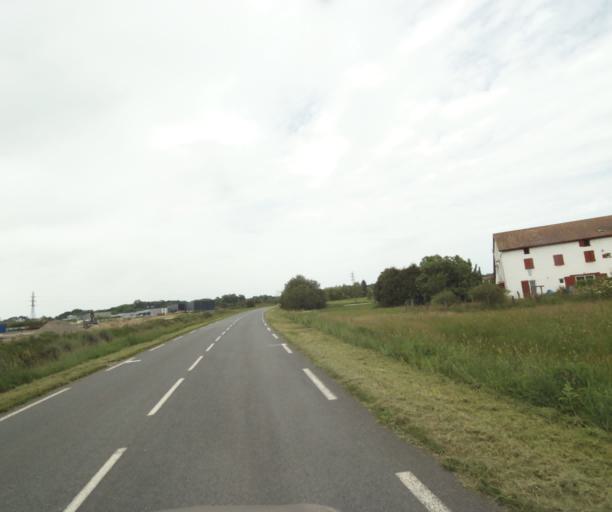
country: FR
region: Aquitaine
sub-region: Departement des Pyrenees-Atlantiques
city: Mouguerre
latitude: 43.4890
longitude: -1.4171
